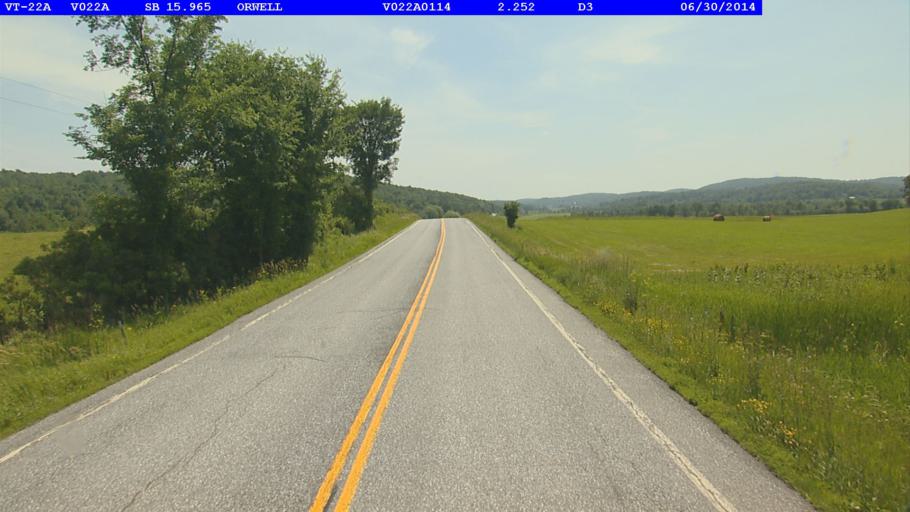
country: US
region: New York
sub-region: Essex County
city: Ticonderoga
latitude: 43.7895
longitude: -73.3067
